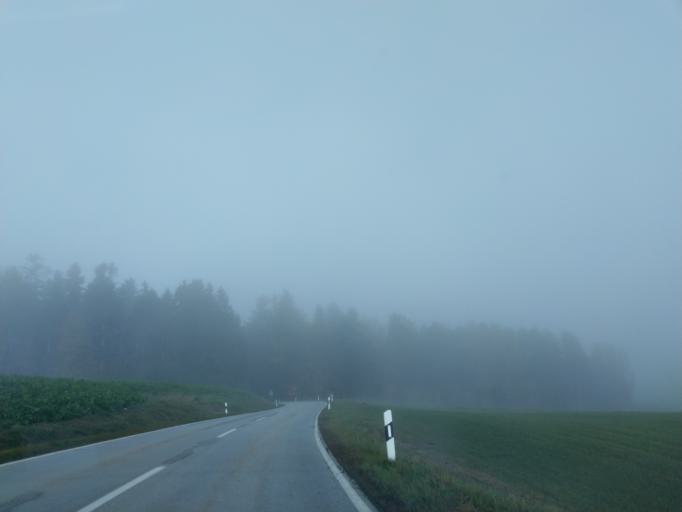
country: DE
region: Bavaria
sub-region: Lower Bavaria
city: Schollnach
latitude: 48.7443
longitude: 13.1893
